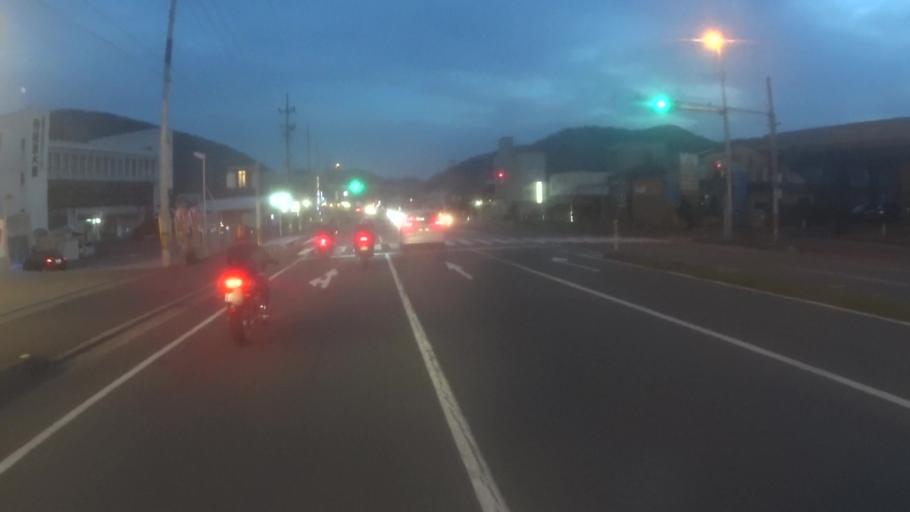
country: JP
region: Kyoto
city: Ayabe
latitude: 35.1614
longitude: 135.4255
